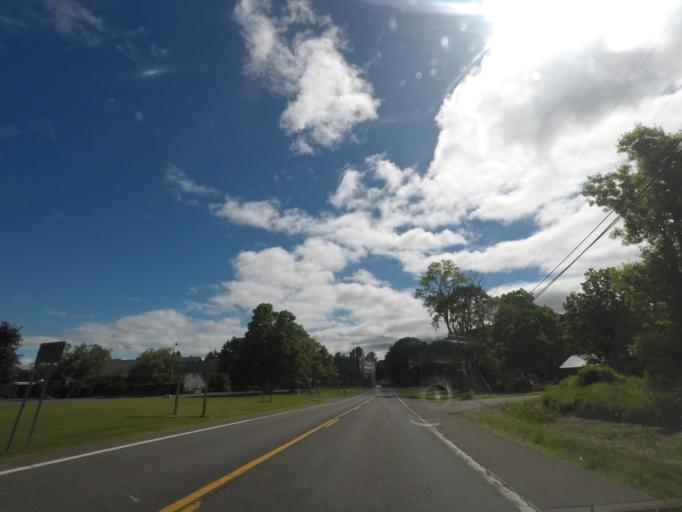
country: US
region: Massachusetts
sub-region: Berkshire County
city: Sheffield
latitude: 42.1183
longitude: -73.5293
